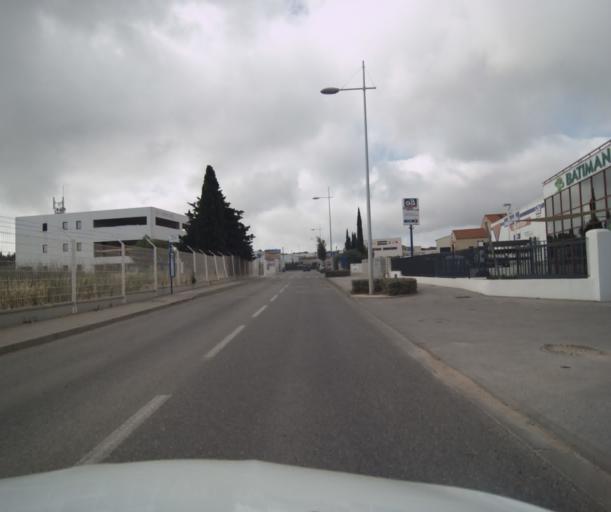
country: FR
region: Provence-Alpes-Cote d'Azur
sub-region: Departement du Var
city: Six-Fours-les-Plages
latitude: 43.1157
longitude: 5.8488
